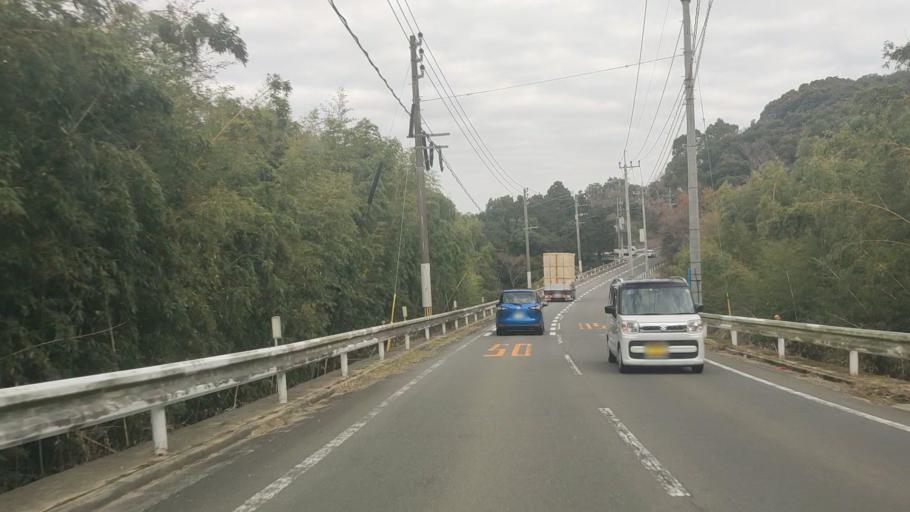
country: JP
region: Nagasaki
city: Shimabara
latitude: 32.8447
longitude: 130.2150
